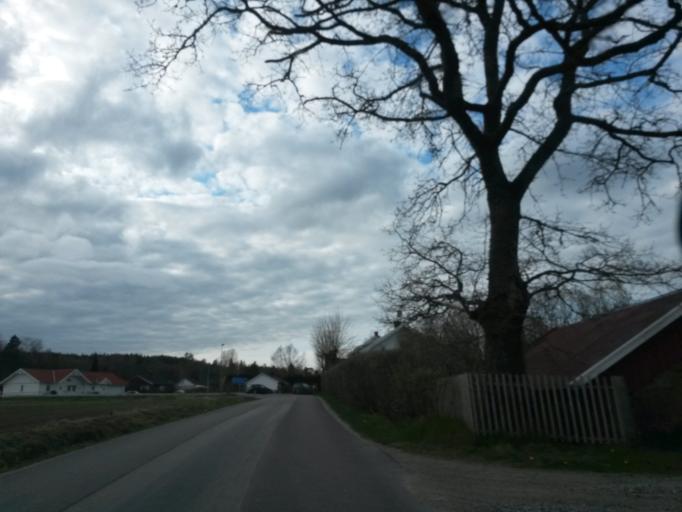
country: SE
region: Vaestra Goetaland
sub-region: Vargarda Kommun
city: Jonstorp
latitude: 58.0214
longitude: 12.6402
